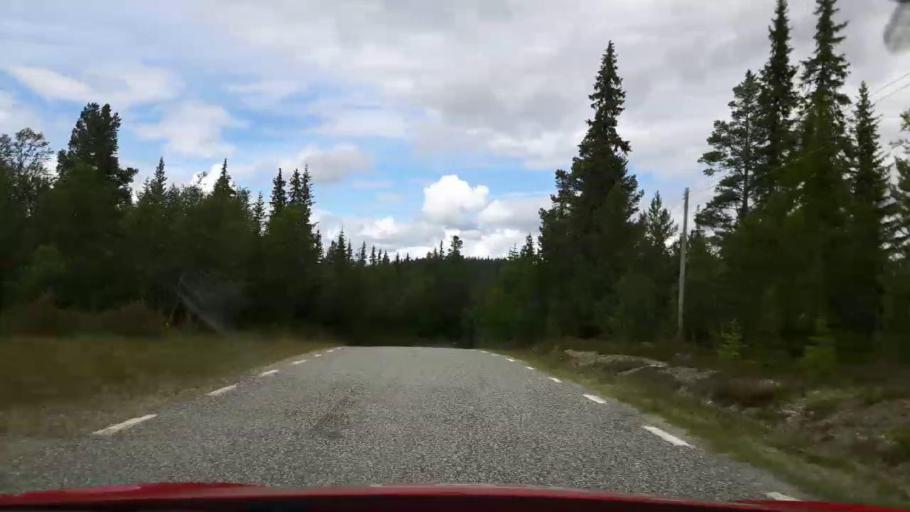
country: NO
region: Hedmark
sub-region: Engerdal
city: Engerdal
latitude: 62.3559
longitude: 12.7941
